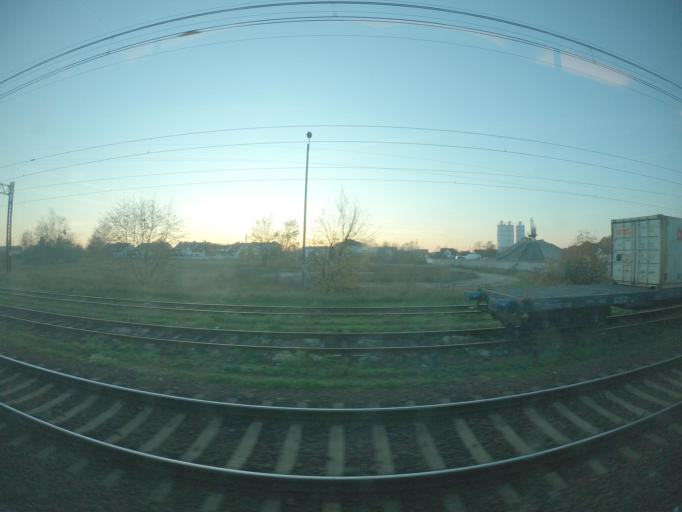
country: PL
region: Lubusz
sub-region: Powiat gorzowski
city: Kostrzyn nad Odra
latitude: 52.6019
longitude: 14.6464
